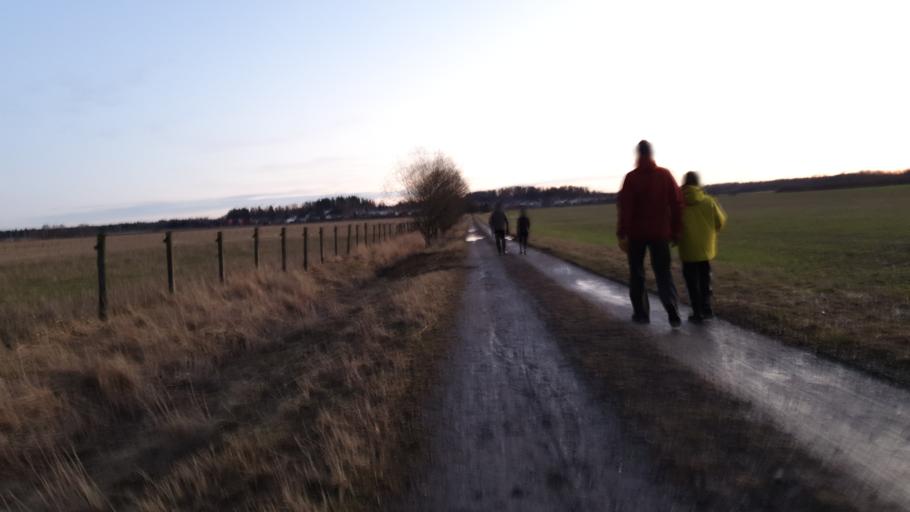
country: FI
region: Uusimaa
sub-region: Helsinki
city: Vantaa
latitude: 60.2737
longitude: 24.9471
